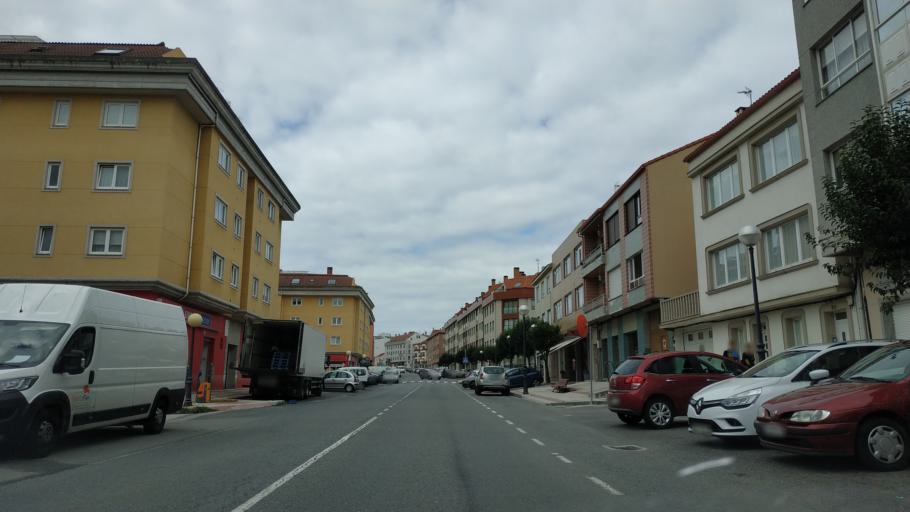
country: ES
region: Galicia
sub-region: Provincia da Coruna
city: Arteixo
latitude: 43.3020
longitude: -8.5123
